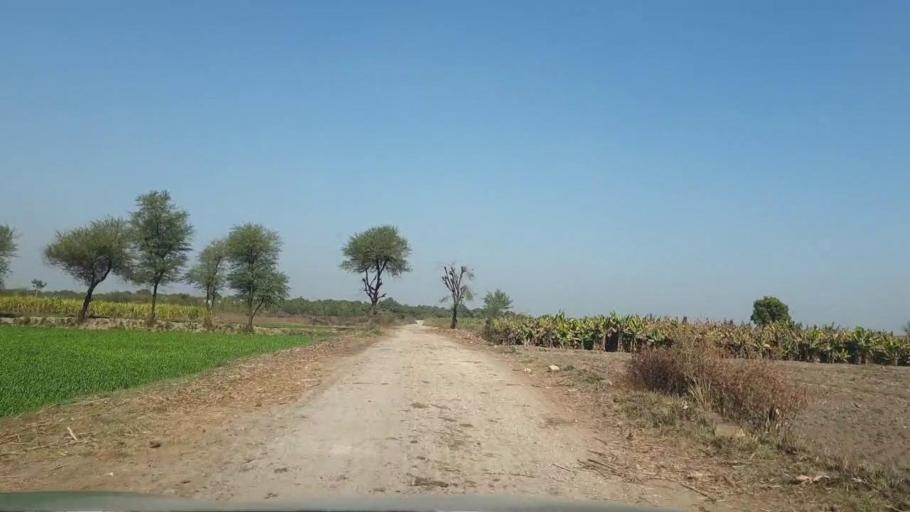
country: PK
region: Sindh
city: Tando Adam
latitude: 25.6177
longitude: 68.6462
